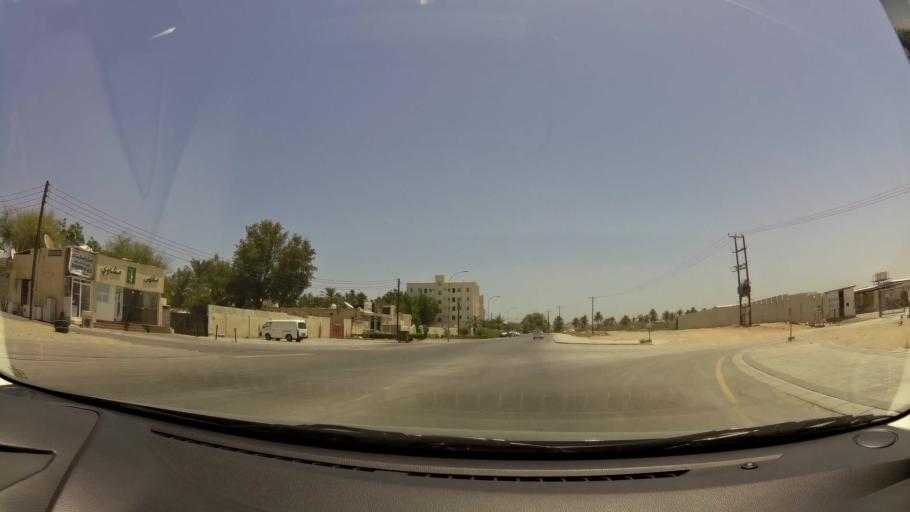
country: OM
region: Muhafazat Masqat
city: As Sib al Jadidah
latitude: 23.6228
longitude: 58.2439
